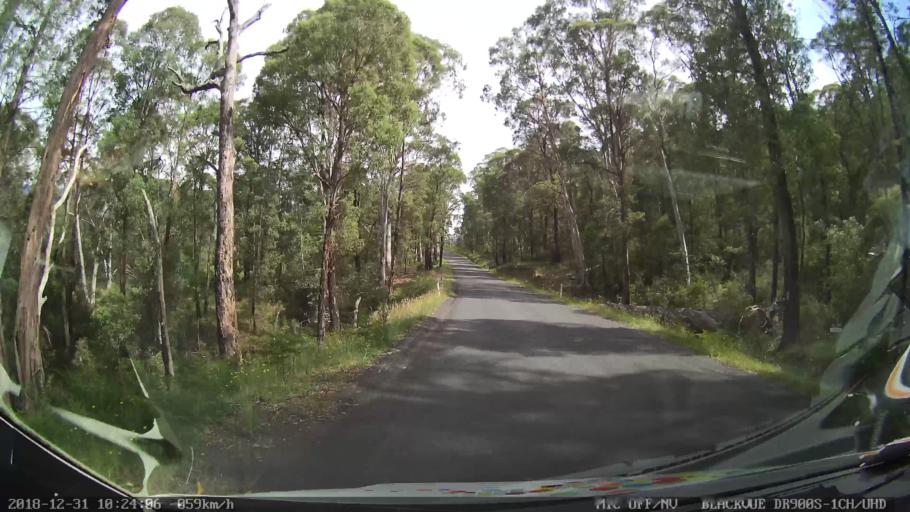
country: AU
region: New South Wales
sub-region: Snowy River
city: Jindabyne
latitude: -36.5150
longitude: 148.1409
